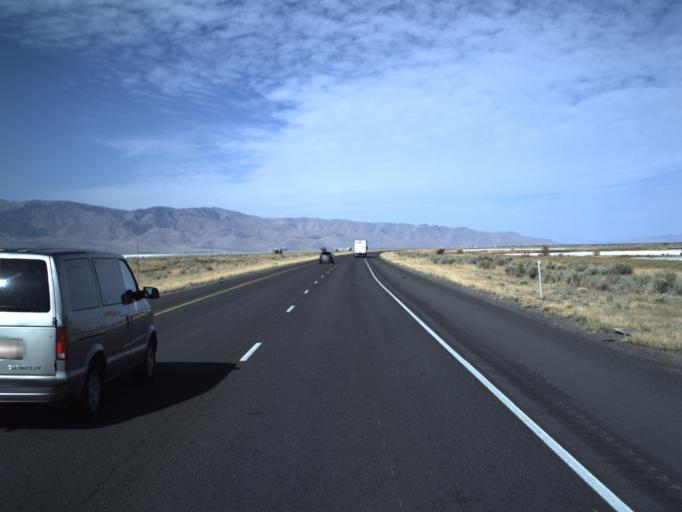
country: US
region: Utah
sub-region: Tooele County
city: Stansbury park
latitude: 40.6629
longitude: -112.3487
